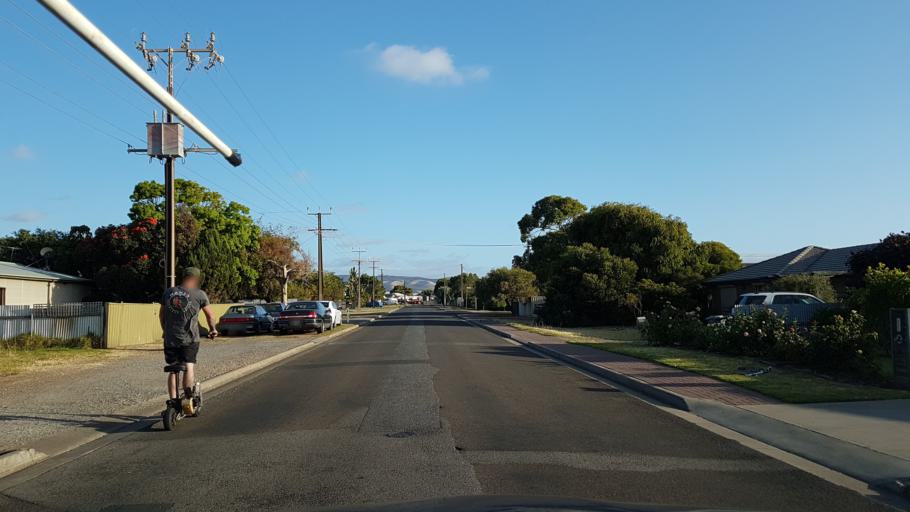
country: AU
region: South Australia
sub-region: Onkaparinga
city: Port Willunga
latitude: -35.2761
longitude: 138.4515
